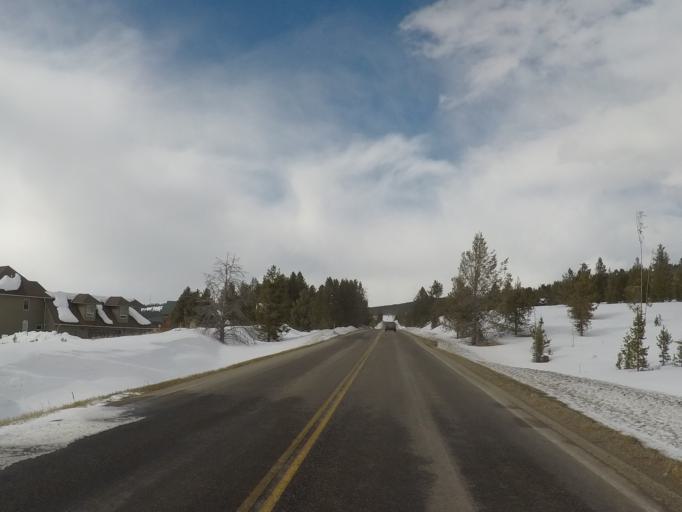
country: US
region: Montana
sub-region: Granite County
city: Philipsburg
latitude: 46.1988
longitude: -113.2689
